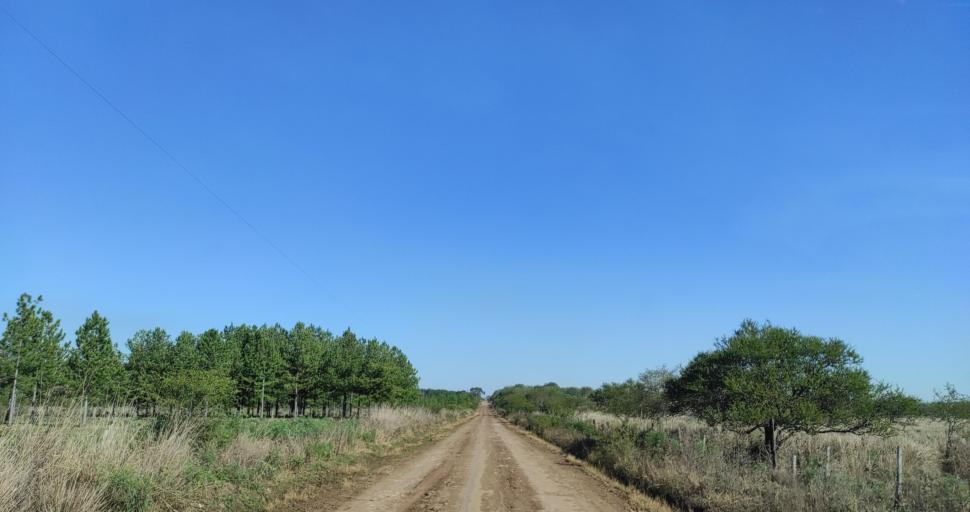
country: AR
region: Misiones
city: Cerro Cora
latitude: -27.6433
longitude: -55.6567
